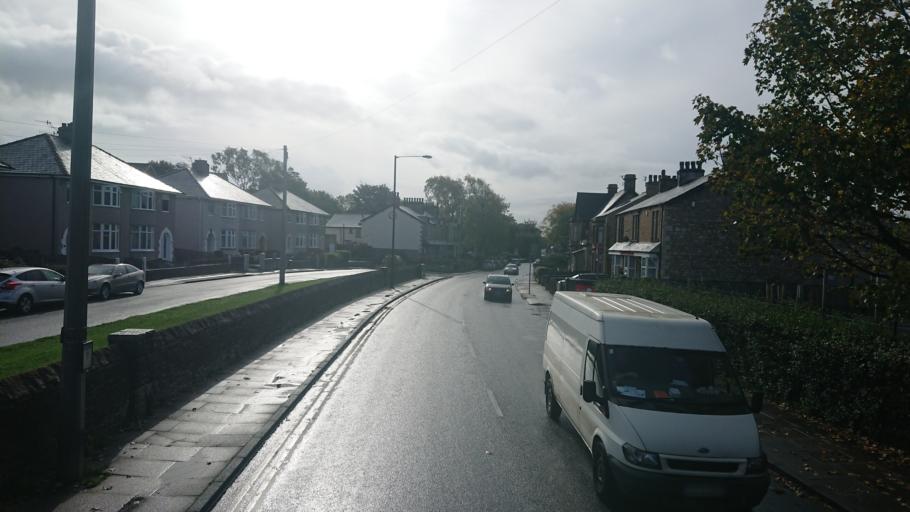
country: GB
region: England
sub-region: Lancashire
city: Lancaster
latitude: 54.0638
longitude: -2.8010
